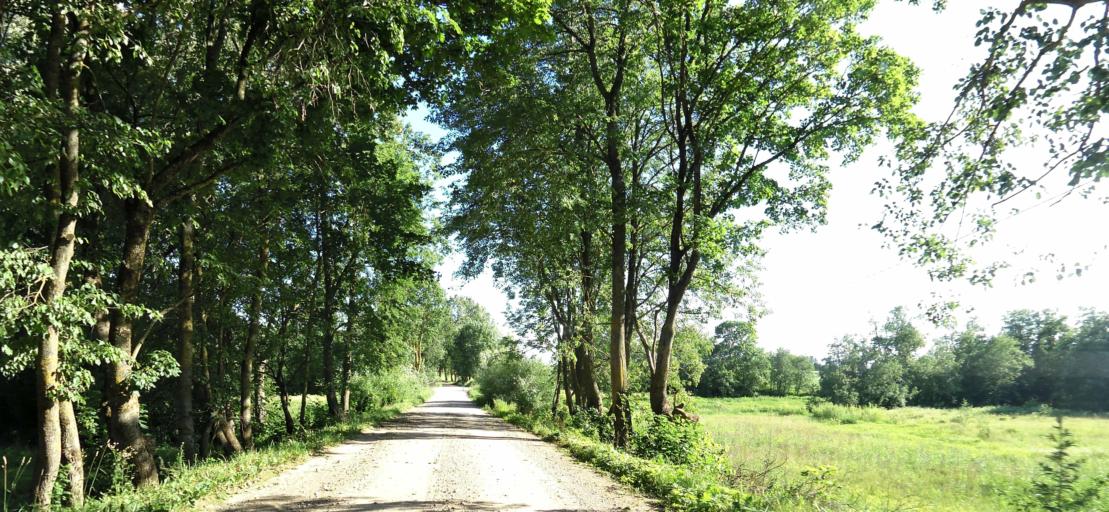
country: LT
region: Panevezys
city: Pasvalys
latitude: 56.1350
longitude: 24.4989
